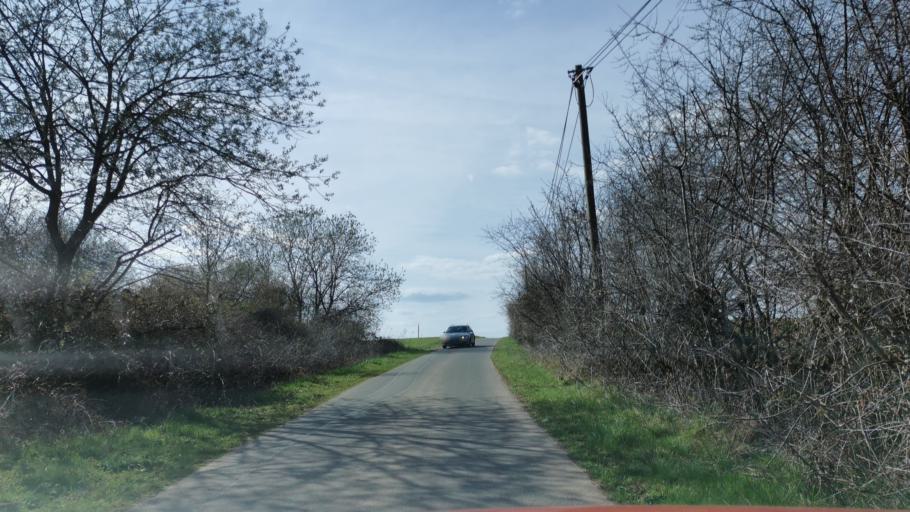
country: DE
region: Rheinland-Pfalz
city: Bruch
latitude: 49.9595
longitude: 6.7665
